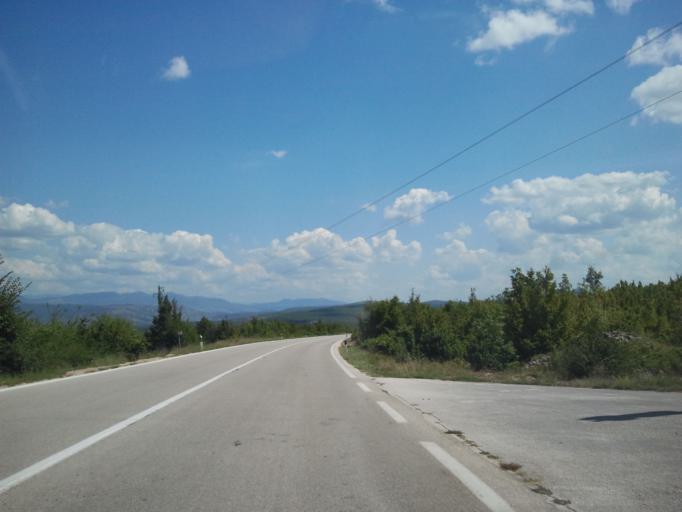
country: HR
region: Zadarska
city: Obrovac
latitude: 44.1972
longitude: 15.6645
